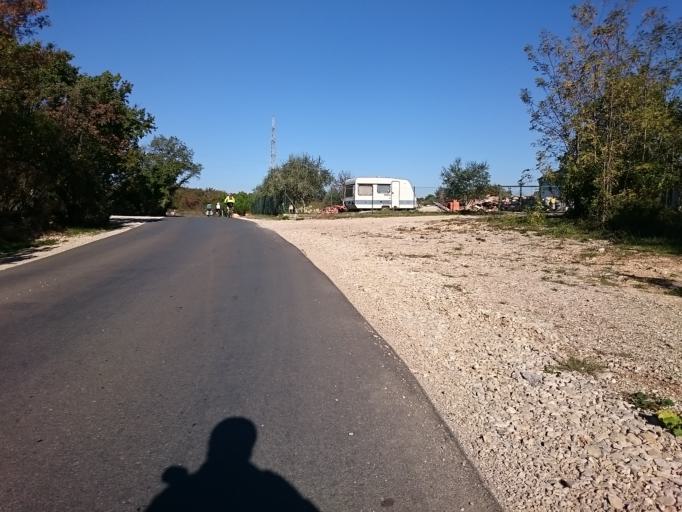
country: HR
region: Istarska
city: Umag
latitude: 45.4574
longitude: 13.5397
